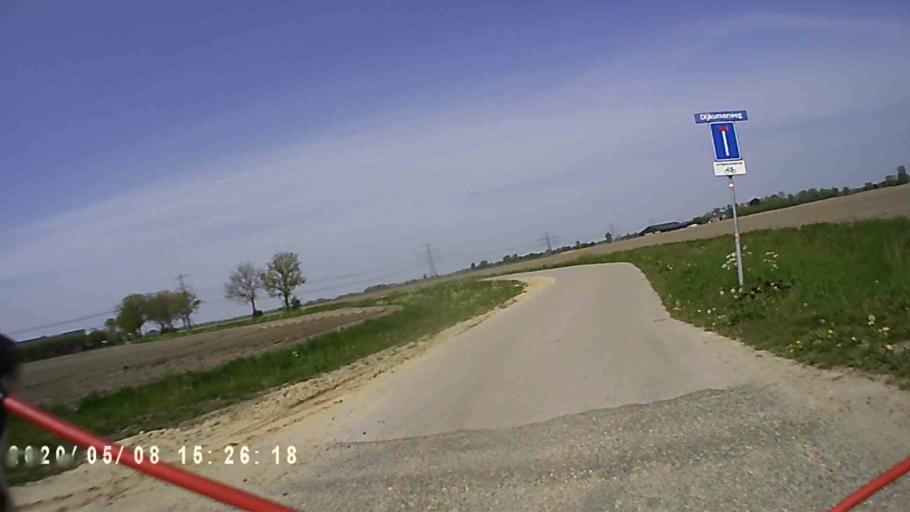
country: NL
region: Groningen
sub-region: Gemeente Appingedam
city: Appingedam
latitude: 53.3577
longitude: 6.7520
